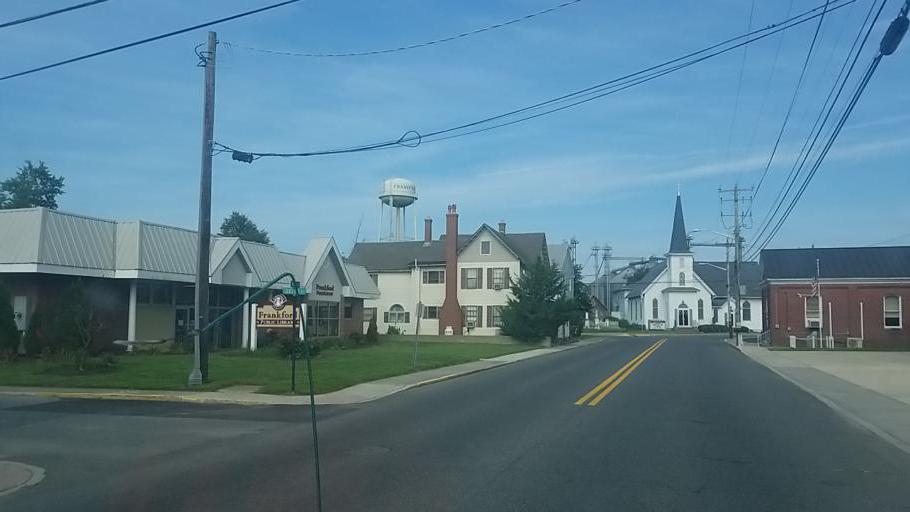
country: US
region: Delaware
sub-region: Sussex County
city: Selbyville
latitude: 38.5173
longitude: -75.2343
